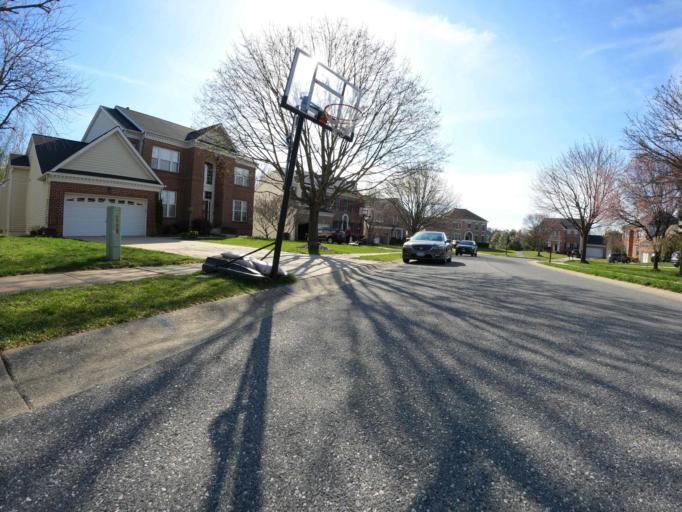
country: US
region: Maryland
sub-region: Howard County
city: Ellicott City
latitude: 39.3021
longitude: -76.8129
